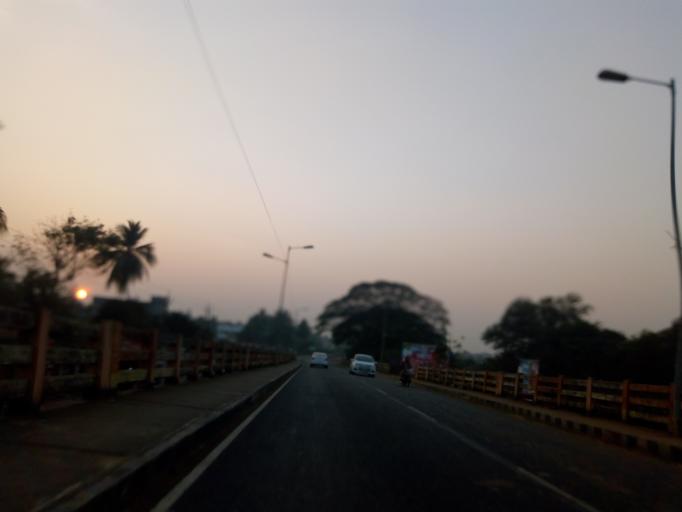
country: IN
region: Andhra Pradesh
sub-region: West Godavari
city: Tadepallegudem
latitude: 16.8108
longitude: 81.5152
